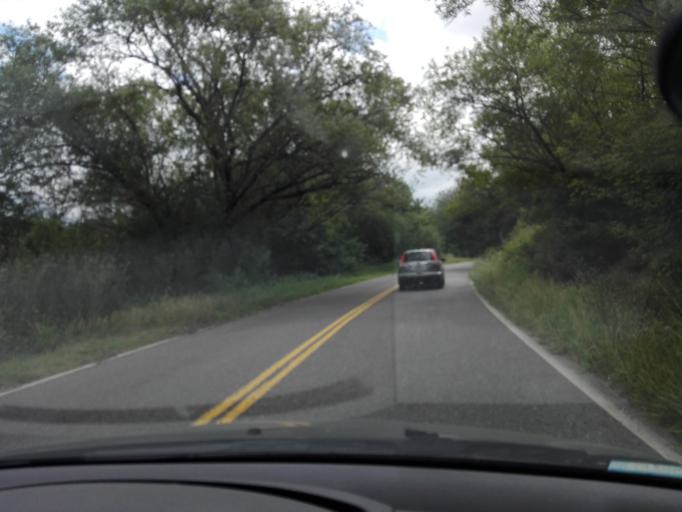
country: AR
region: Cordoba
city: Cuesta Blanca
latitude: -31.6053
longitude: -64.5543
